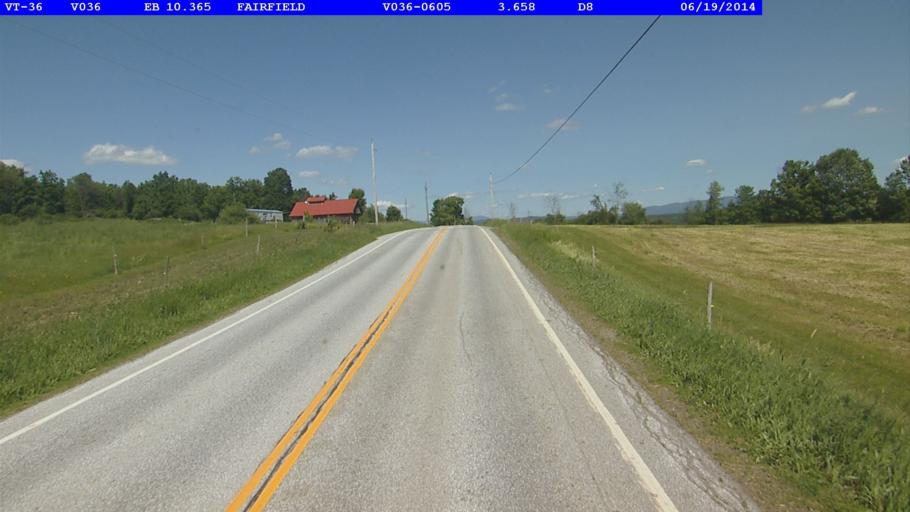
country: US
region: Vermont
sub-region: Franklin County
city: Saint Albans
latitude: 44.7981
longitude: -72.9608
